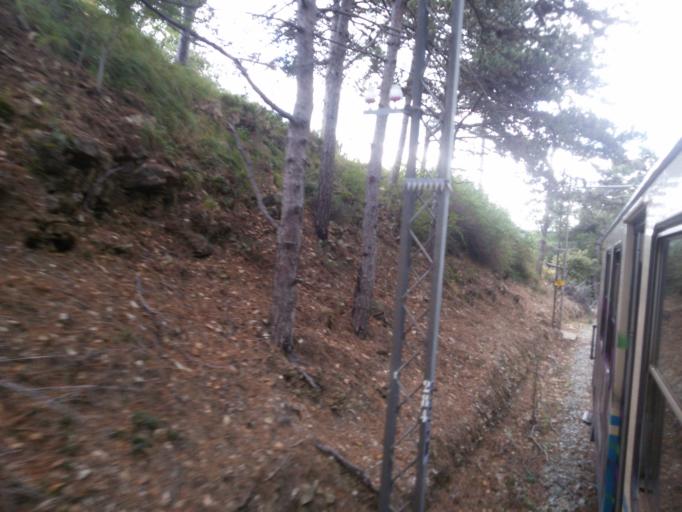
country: IT
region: Liguria
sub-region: Provincia di Genova
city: Genoa
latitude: 44.4440
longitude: 8.9425
